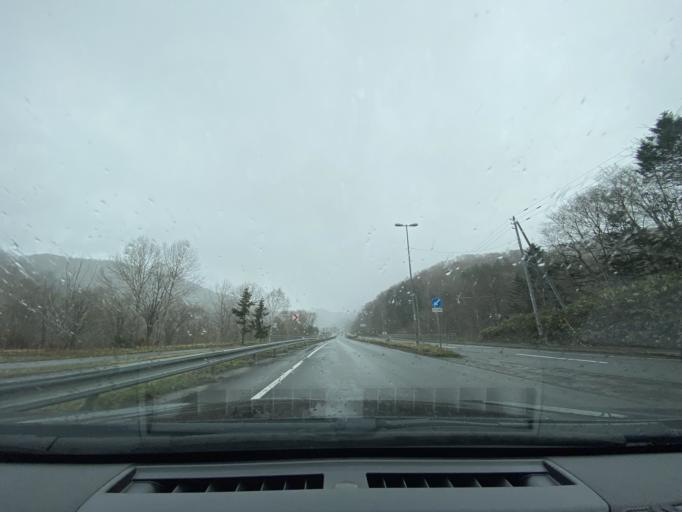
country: JP
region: Hokkaido
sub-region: Asahikawa-shi
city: Asahikawa
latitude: 43.7319
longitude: 142.2284
